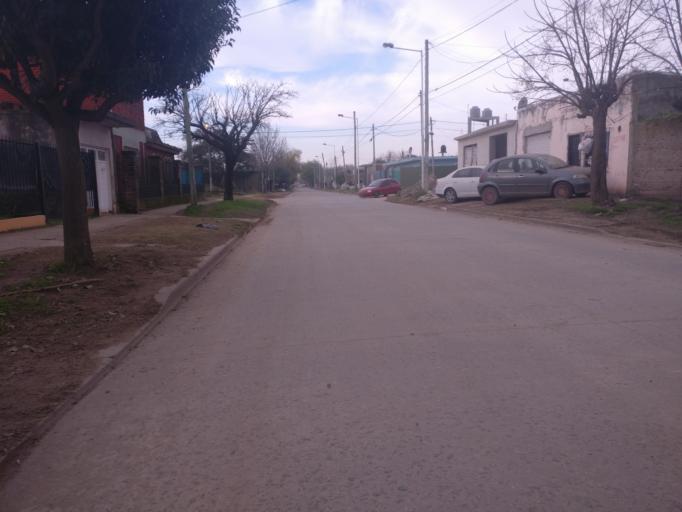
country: AR
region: Buenos Aires
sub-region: Partido de Ezeiza
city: Ezeiza
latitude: -34.9404
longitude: -58.6117
